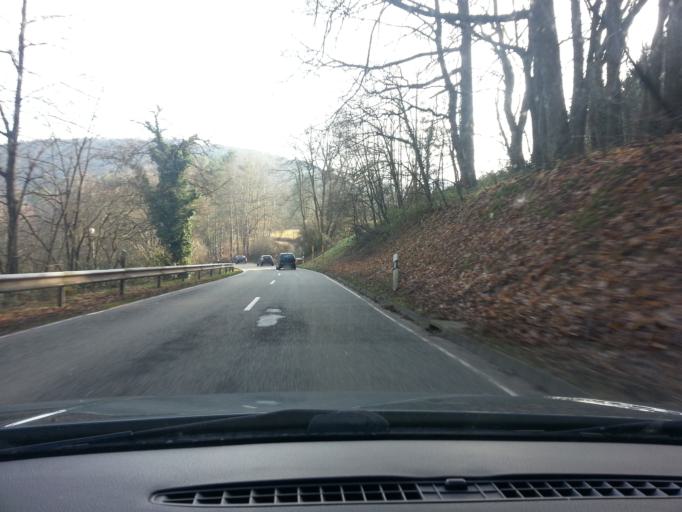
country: DE
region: Rheinland-Pfalz
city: Schwanheim
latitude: 49.1824
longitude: 7.8777
